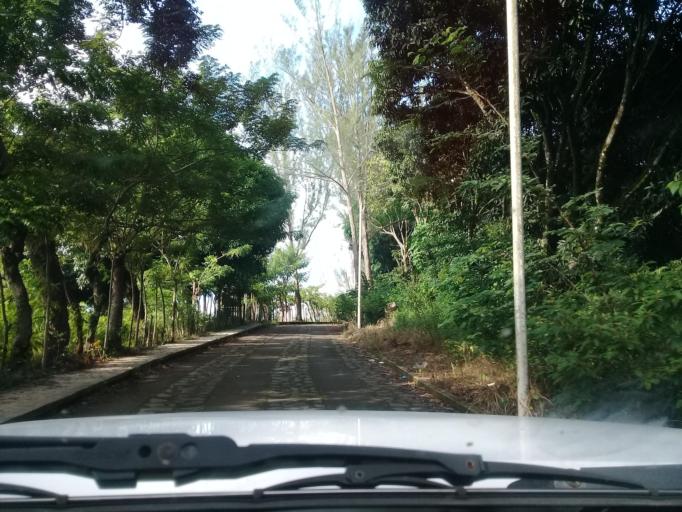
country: MX
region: Veracruz
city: Catemaco
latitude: 18.4304
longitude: -95.1259
